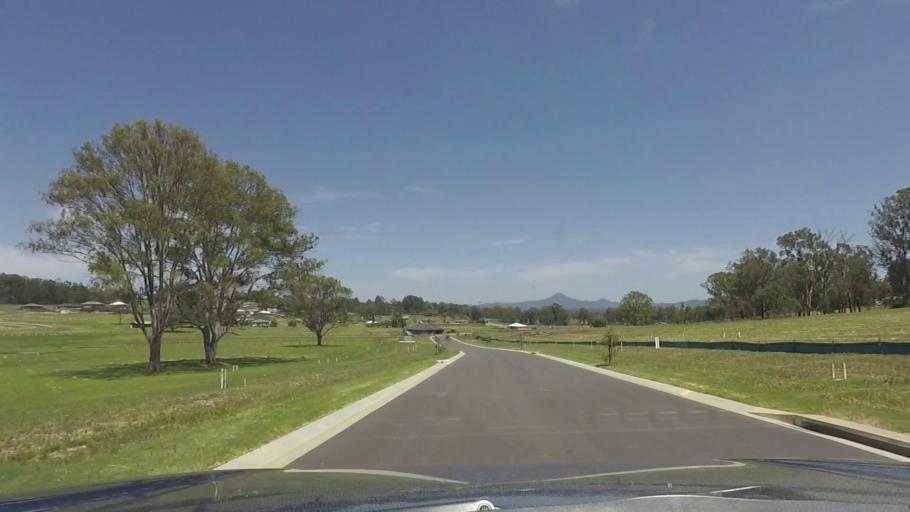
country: AU
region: Queensland
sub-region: Logan
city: Cedar Vale
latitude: -27.8876
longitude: 152.9905
